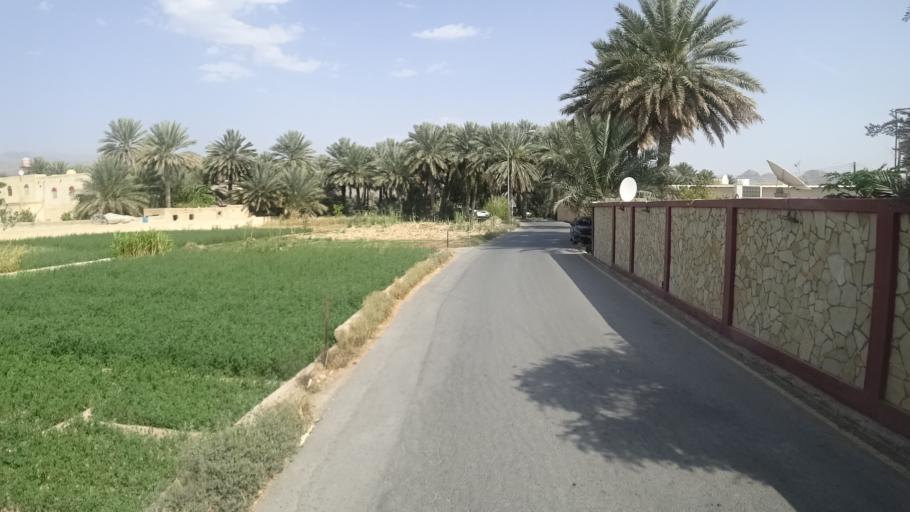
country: OM
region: Muhafazat ad Dakhiliyah
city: Bahla'
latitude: 23.0972
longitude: 57.3074
